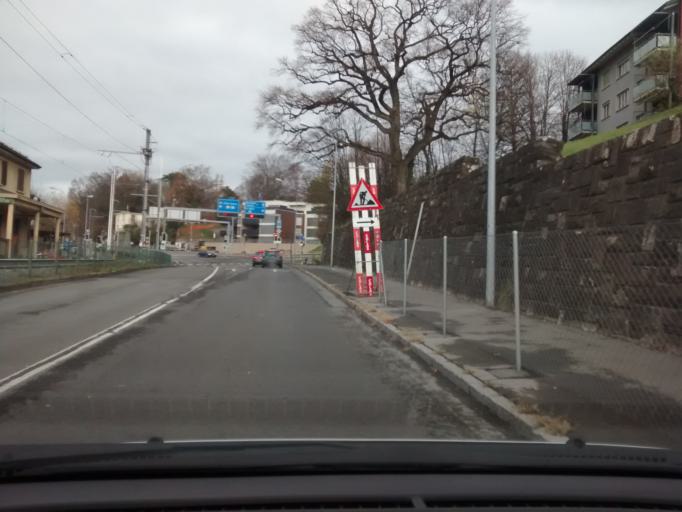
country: CH
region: Vaud
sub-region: Lausanne District
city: Blecherette
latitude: 46.5394
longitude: 6.6077
